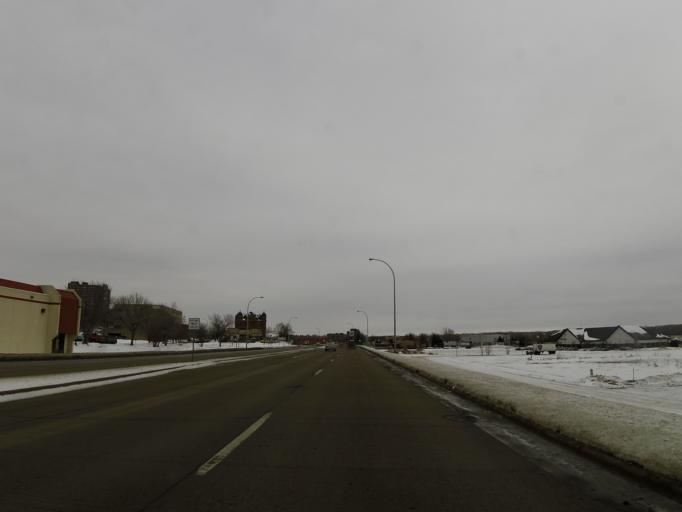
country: US
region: Minnesota
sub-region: Dakota County
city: South Saint Paul
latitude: 44.8901
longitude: -93.0332
